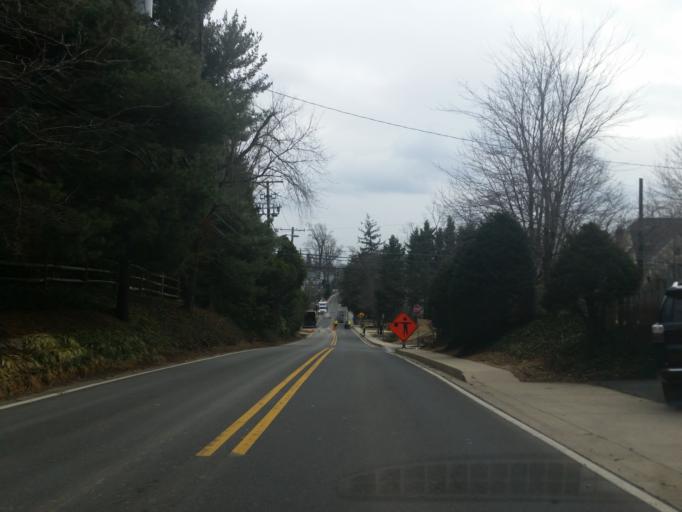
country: US
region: Maryland
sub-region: Montgomery County
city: Chevy Chase
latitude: 38.9829
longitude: -77.0721
